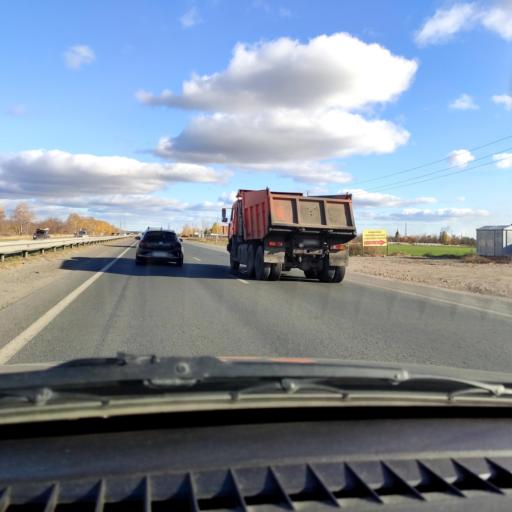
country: RU
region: Samara
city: Tol'yatti
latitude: 53.5780
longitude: 49.4176
